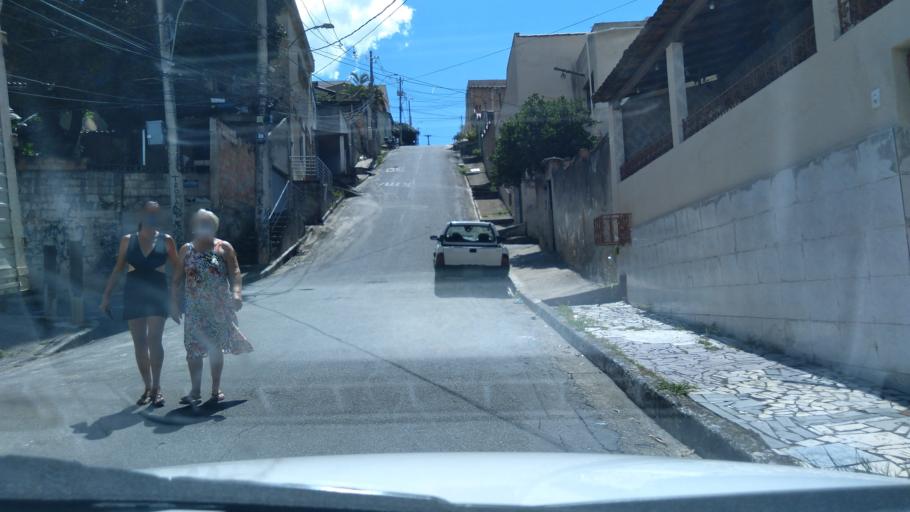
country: BR
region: Minas Gerais
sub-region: Belo Horizonte
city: Belo Horizonte
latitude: -19.8677
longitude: -43.9156
